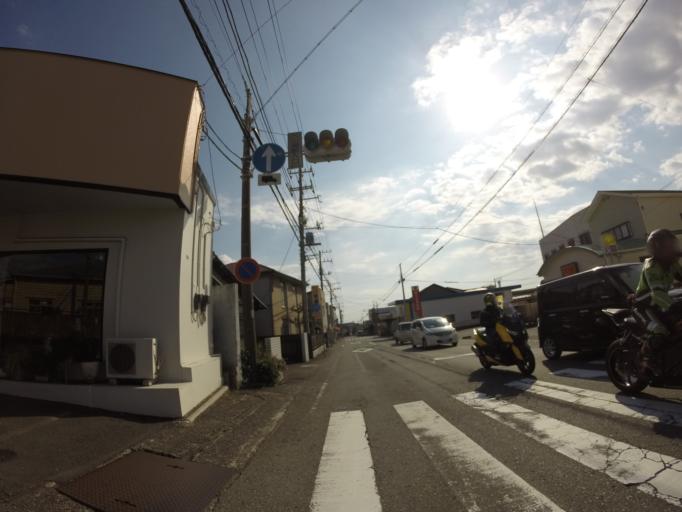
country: JP
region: Shizuoka
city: Fujinomiya
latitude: 35.1874
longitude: 138.6463
